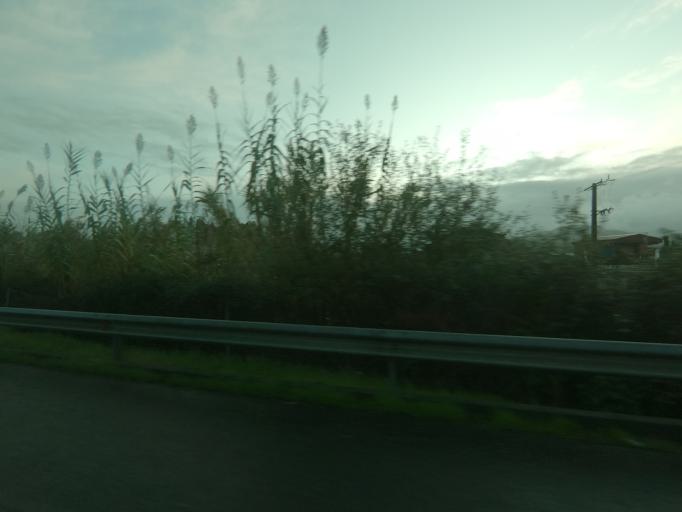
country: ES
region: Galicia
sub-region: Provincia de Pontevedra
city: Tui
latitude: 42.0562
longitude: -8.6543
